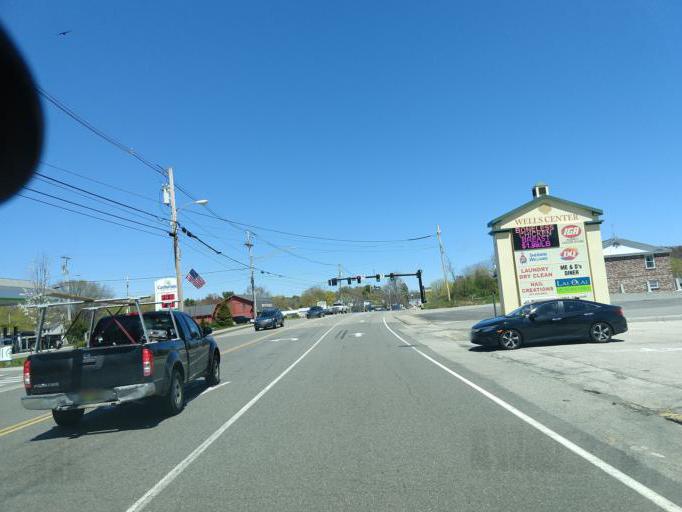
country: US
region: Maine
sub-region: York County
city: Wells Beach Station
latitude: 43.3216
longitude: -70.5812
